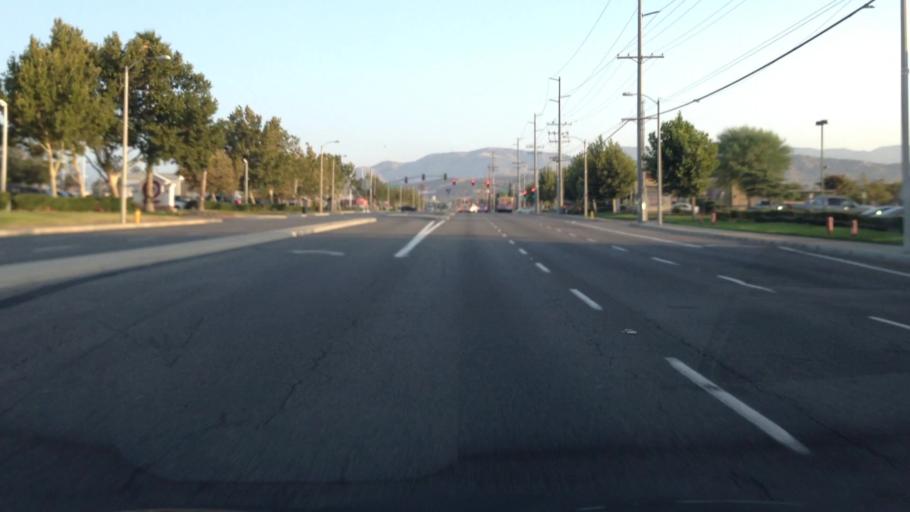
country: US
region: California
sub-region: Los Angeles County
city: Desert View Highlands
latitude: 34.6001
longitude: -118.1478
